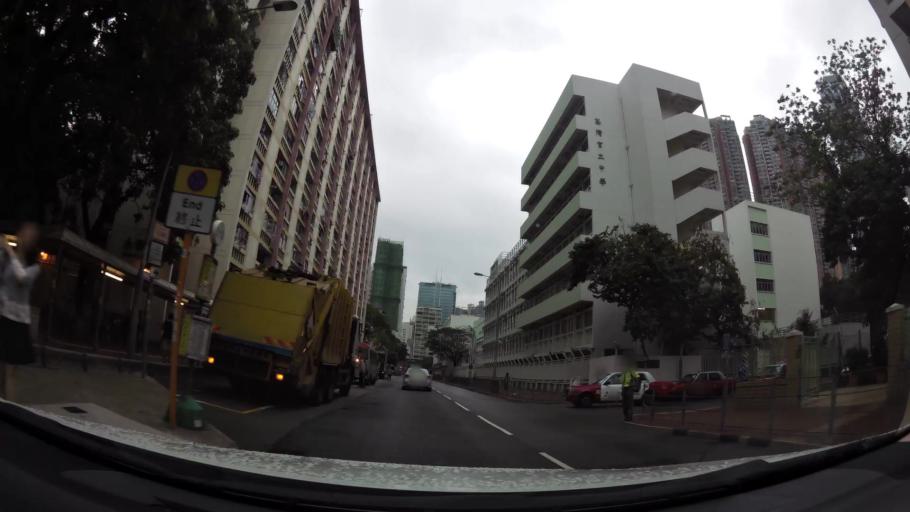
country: HK
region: Tsuen Wan
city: Tsuen Wan
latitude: 22.3733
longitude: 114.1132
